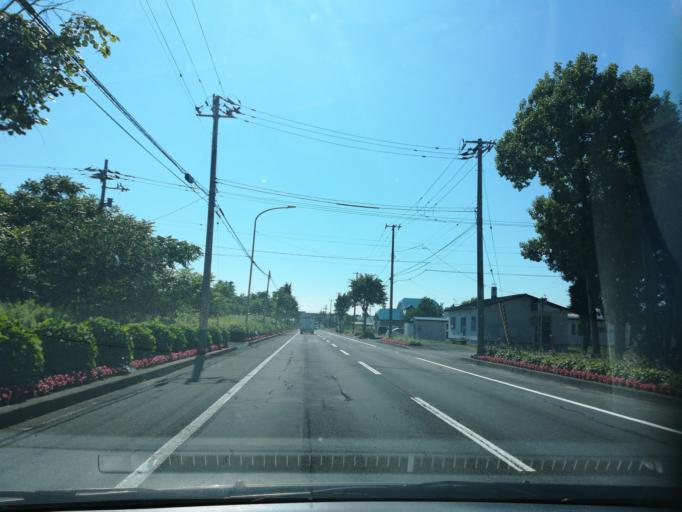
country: JP
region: Hokkaido
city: Chitose
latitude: 42.9157
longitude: 141.8996
